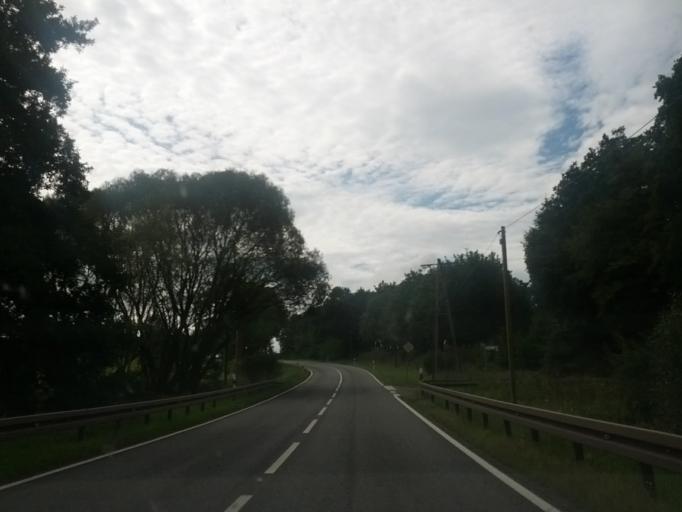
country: DE
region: Thuringia
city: Wolfsburg-Unkeroda
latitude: 50.9056
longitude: 10.3071
